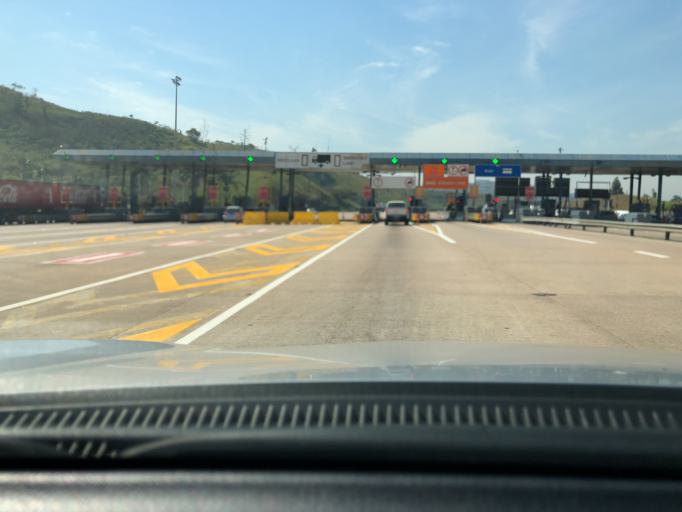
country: ZA
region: KwaZulu-Natal
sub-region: eThekwini Metropolitan Municipality
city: Mpumalanga
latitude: -29.8232
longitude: 30.8021
